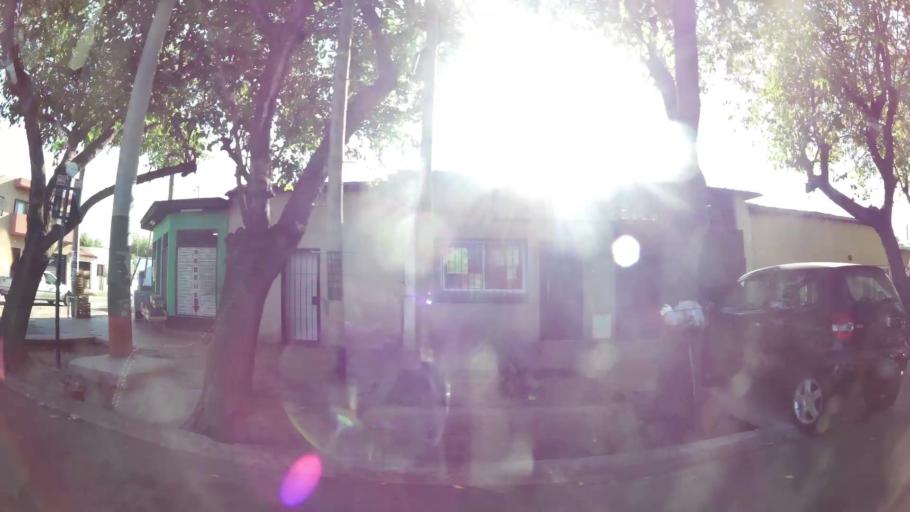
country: AR
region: Mendoza
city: Mendoza
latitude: -32.9085
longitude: -68.8288
